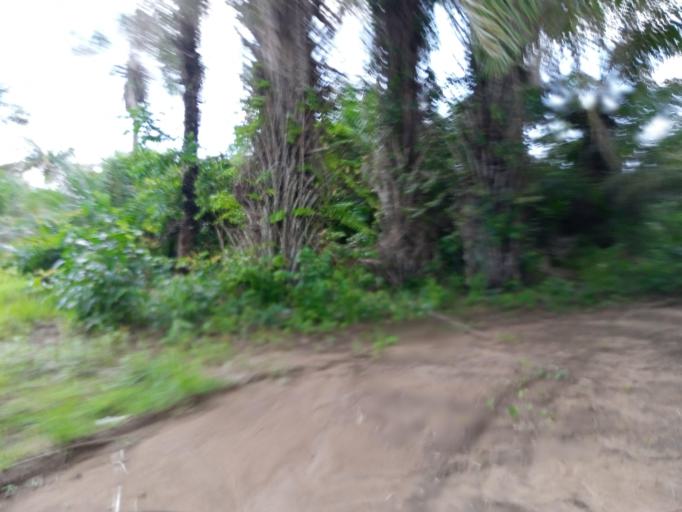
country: SL
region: Northern Province
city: Masoyila
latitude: 8.5822
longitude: -13.1668
